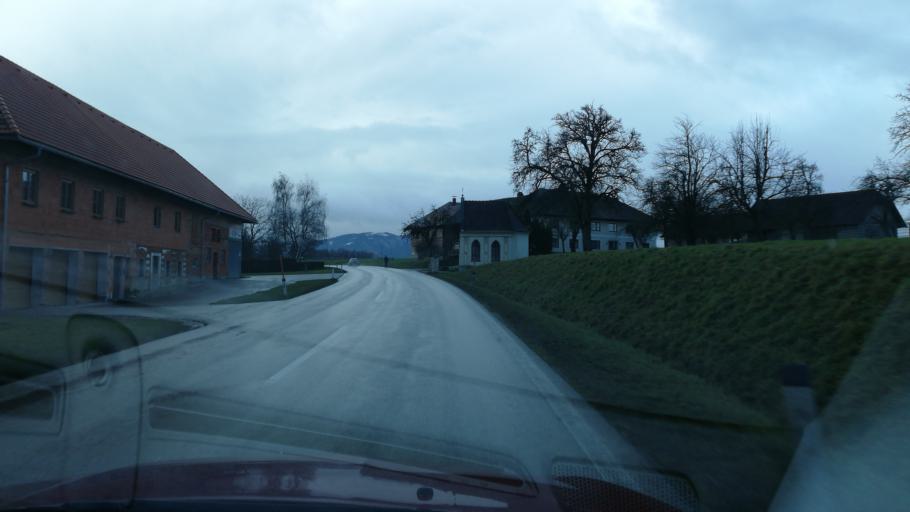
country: AT
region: Upper Austria
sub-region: Politischer Bezirk Kirchdorf an der Krems
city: Kremsmunster
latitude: 47.9919
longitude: 14.0794
